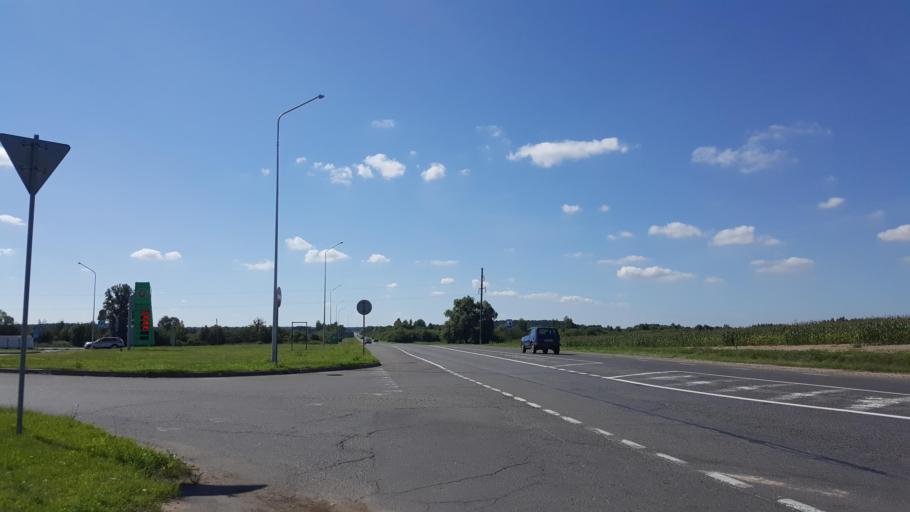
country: BY
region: Brest
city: Kamyanyets
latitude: 52.3982
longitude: 23.7858
